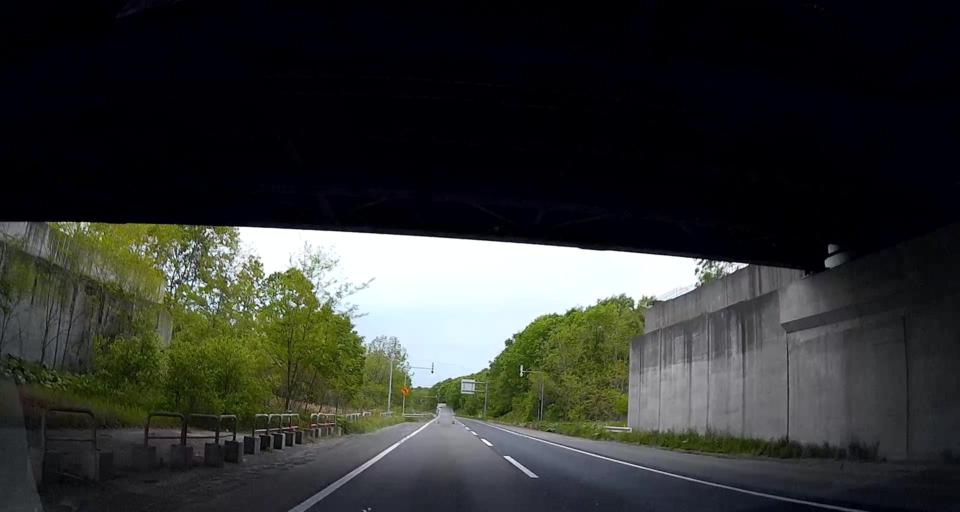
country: JP
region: Hokkaido
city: Chitose
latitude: 42.7098
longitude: 141.7470
